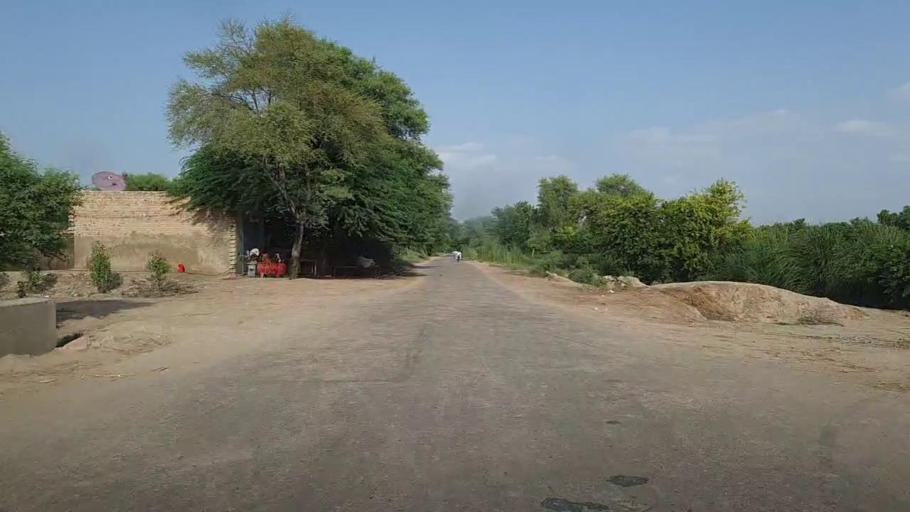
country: PK
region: Sindh
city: Khairpur
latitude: 28.0754
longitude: 69.8115
